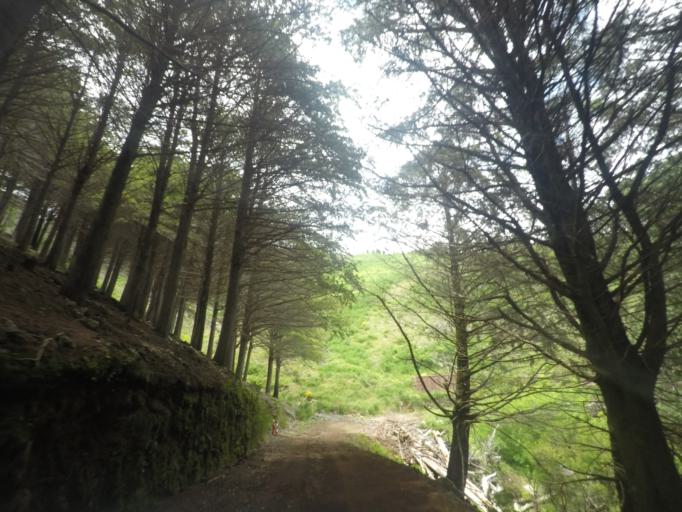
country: PT
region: Madeira
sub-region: Funchal
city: Nossa Senhora do Monte
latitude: 32.7062
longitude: -16.9041
